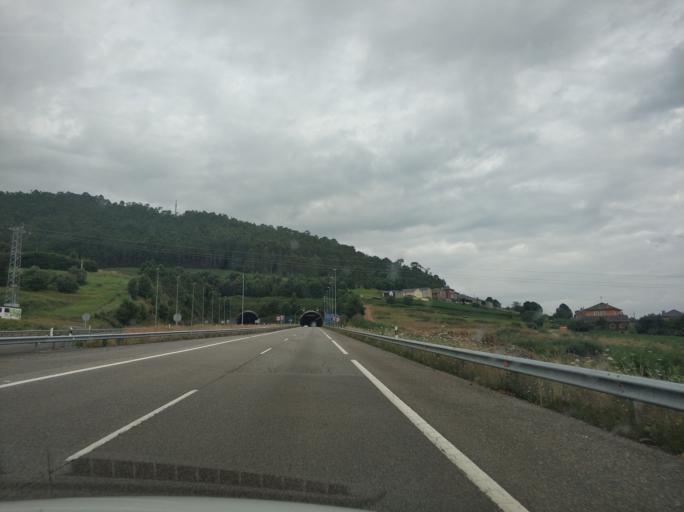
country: ES
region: Asturias
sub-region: Province of Asturias
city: Coana
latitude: 43.5343
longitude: -6.7440
